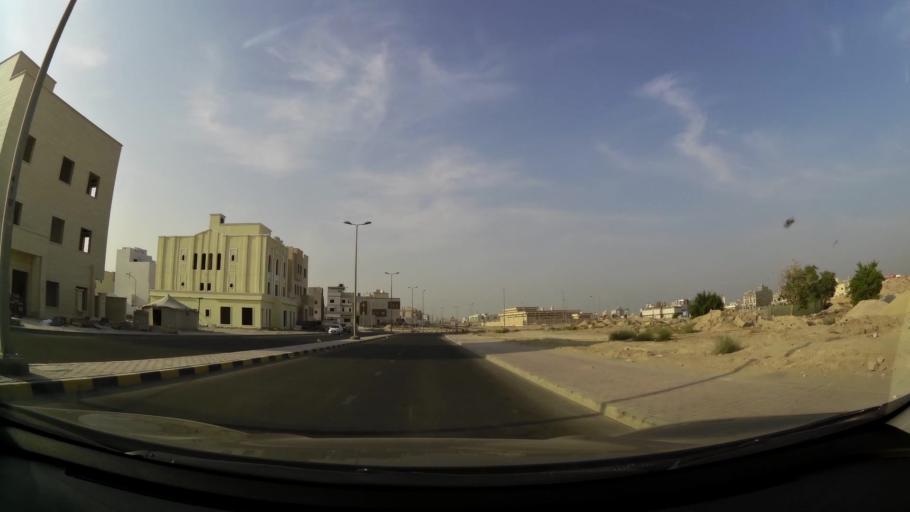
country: KW
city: Al Funaytis
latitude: 29.2243
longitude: 48.0915
